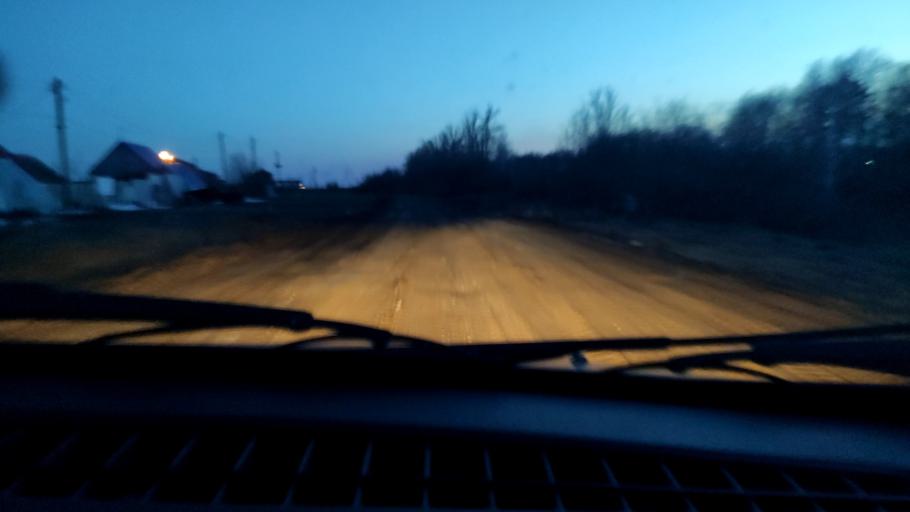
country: RU
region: Bashkortostan
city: Iglino
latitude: 54.7953
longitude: 56.3106
